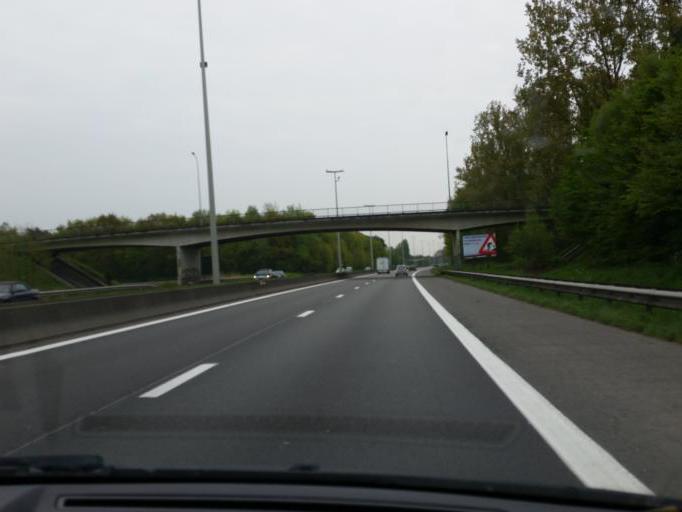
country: BE
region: Flanders
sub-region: Provincie Oost-Vlaanderen
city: Melle
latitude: 51.0176
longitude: 3.8026
